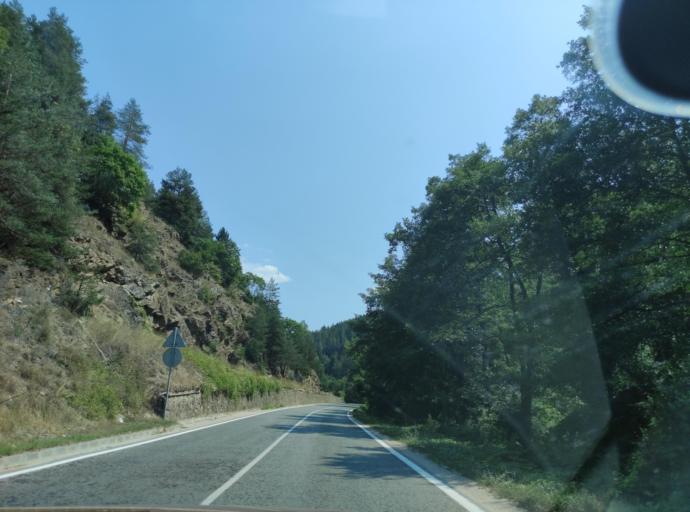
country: BG
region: Blagoevgrad
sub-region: Obshtina Belitsa
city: Belitsa
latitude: 41.8930
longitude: 23.5434
